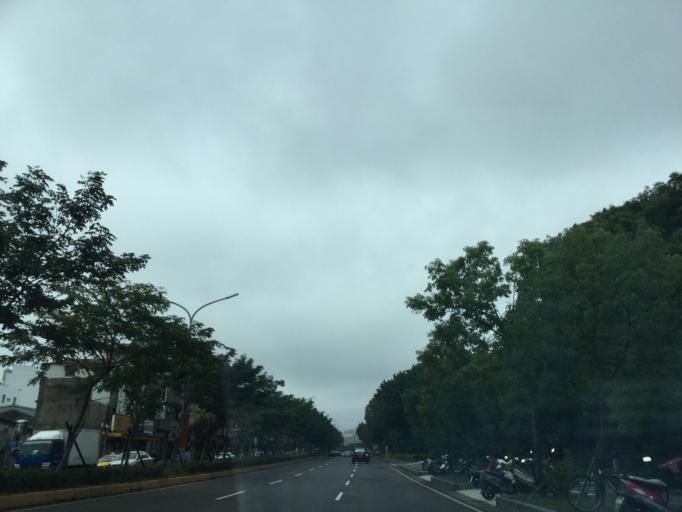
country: TW
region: Taiwan
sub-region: Hsinchu
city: Hsinchu
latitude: 24.7928
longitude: 121.0020
